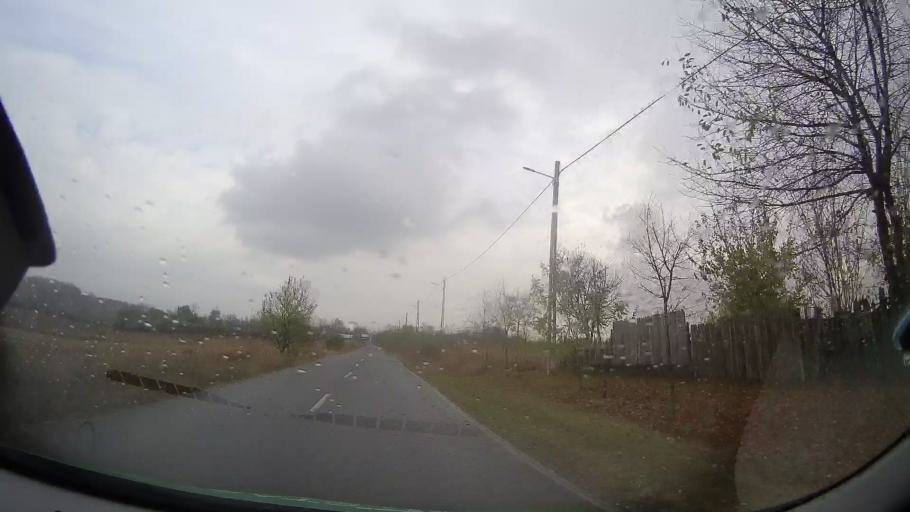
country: RO
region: Prahova
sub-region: Comuna Draganesti
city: Draganesti
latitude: 44.7863
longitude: 26.3163
